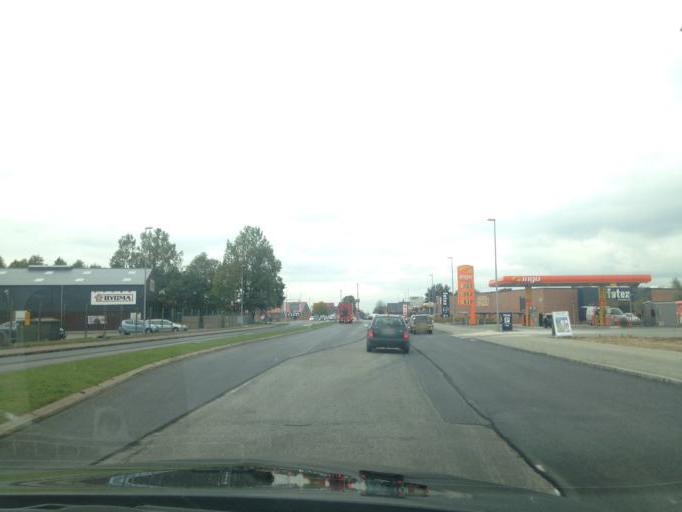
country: DK
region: South Denmark
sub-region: Kolding Kommune
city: Kolding
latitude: 55.4692
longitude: 9.4713
